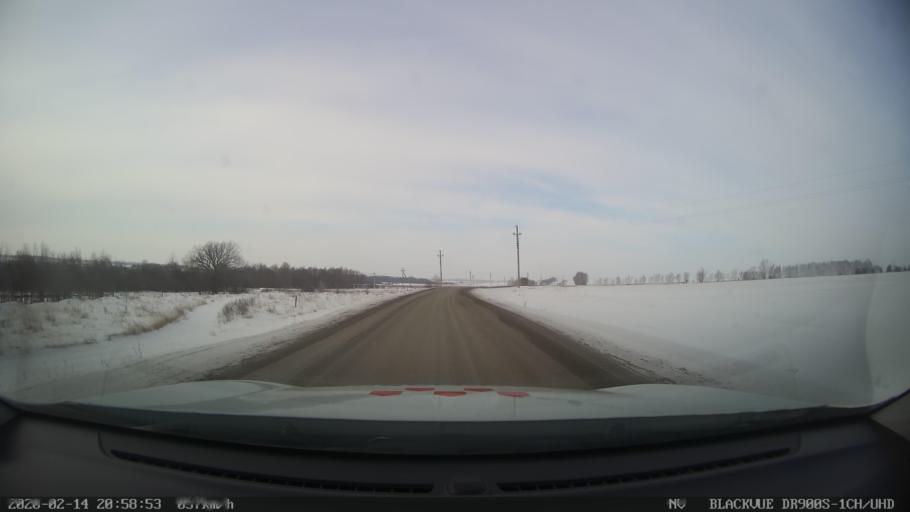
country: RU
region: Tatarstan
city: Kuybyshevskiy Zaton
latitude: 55.1786
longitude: 49.2432
